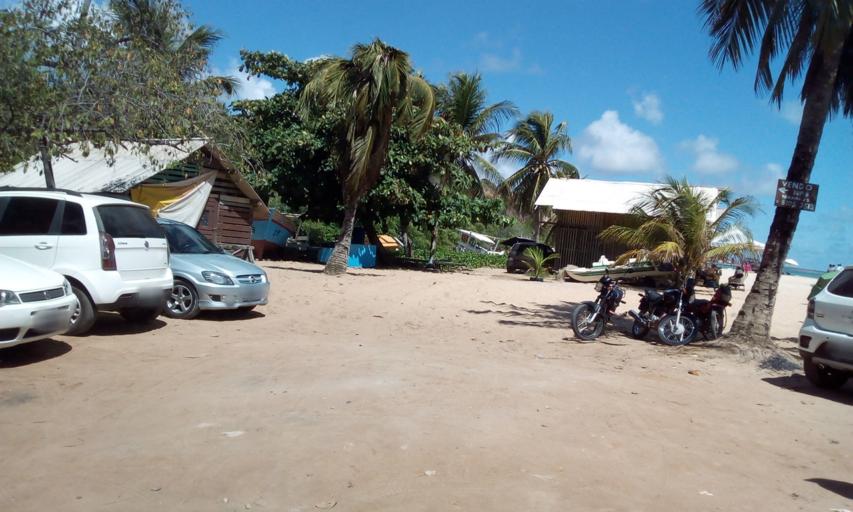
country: BR
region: Paraiba
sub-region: Conde
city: Conde
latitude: -7.2742
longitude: -34.8022
